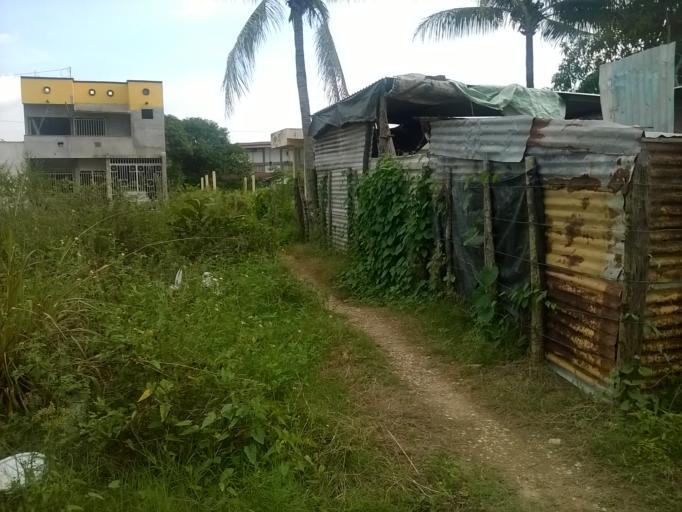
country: MX
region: Tabasco
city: Jalapa
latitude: 17.7249
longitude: -92.8098
